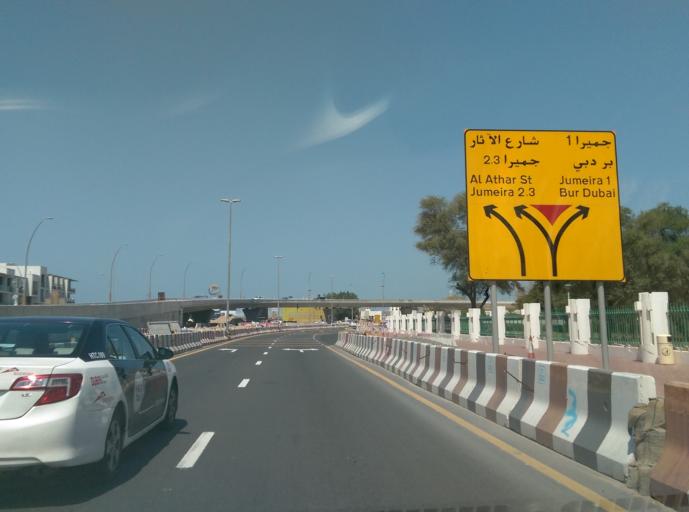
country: AE
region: Dubai
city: Dubai
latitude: 25.1856
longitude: 55.2420
